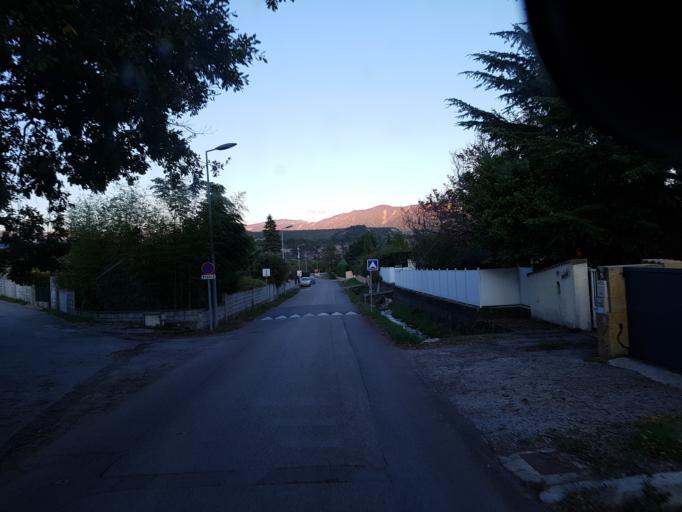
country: FR
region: Provence-Alpes-Cote d'Azur
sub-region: Departement des Alpes-de-Haute-Provence
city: Peipin
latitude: 44.1314
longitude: 5.9716
